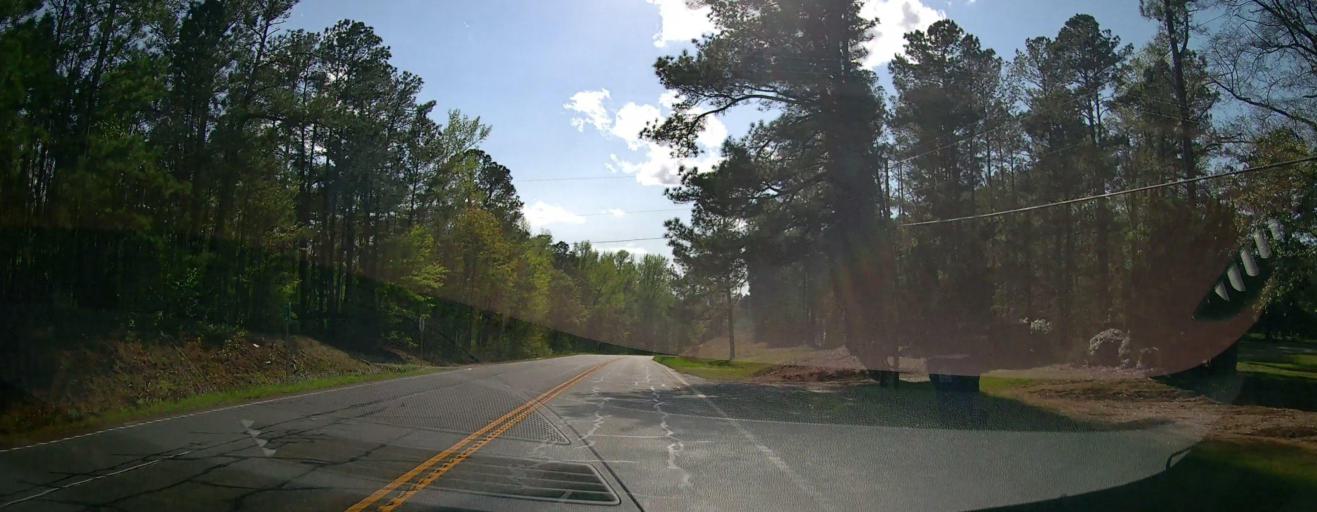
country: US
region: Georgia
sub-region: Baldwin County
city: Hardwick
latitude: 33.0906
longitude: -83.1876
